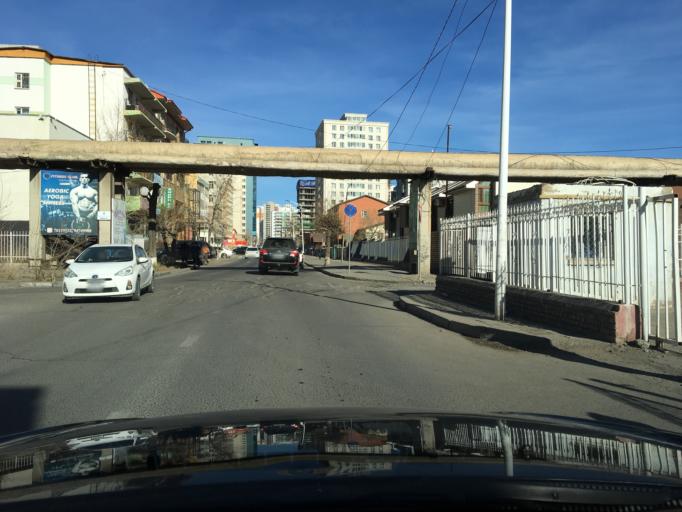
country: MN
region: Ulaanbaatar
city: Ulaanbaatar
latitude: 47.8956
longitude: 106.8962
